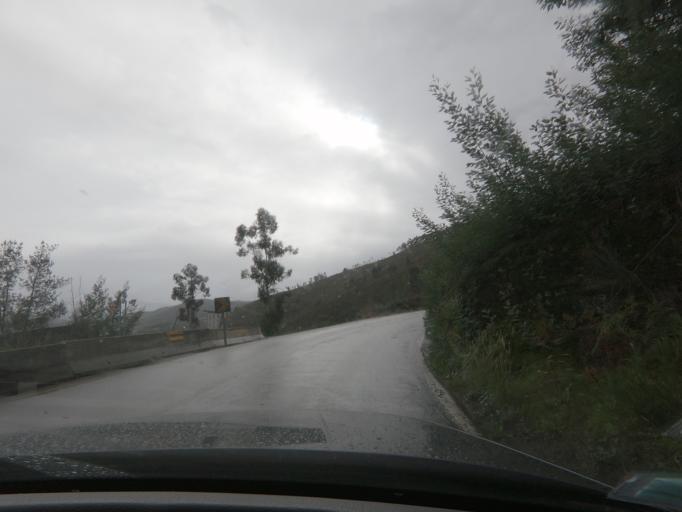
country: PT
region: Vila Real
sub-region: Mondim de Basto
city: Mondim de Basto
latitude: 41.4092
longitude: -7.9669
